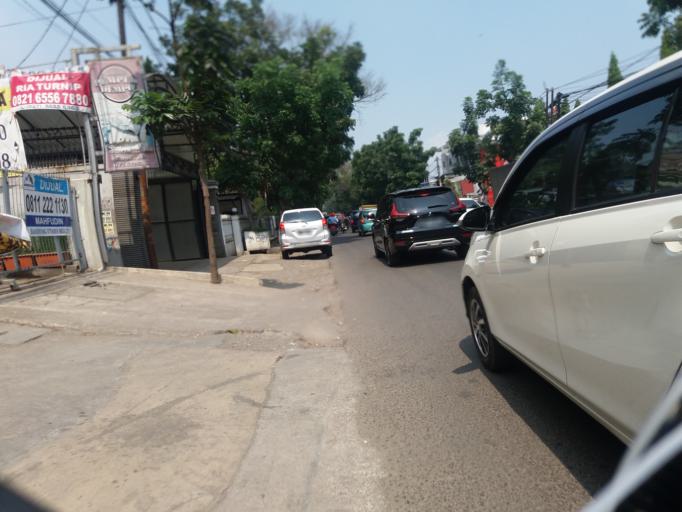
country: ID
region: West Java
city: Bandung
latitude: -6.9094
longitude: 107.5786
